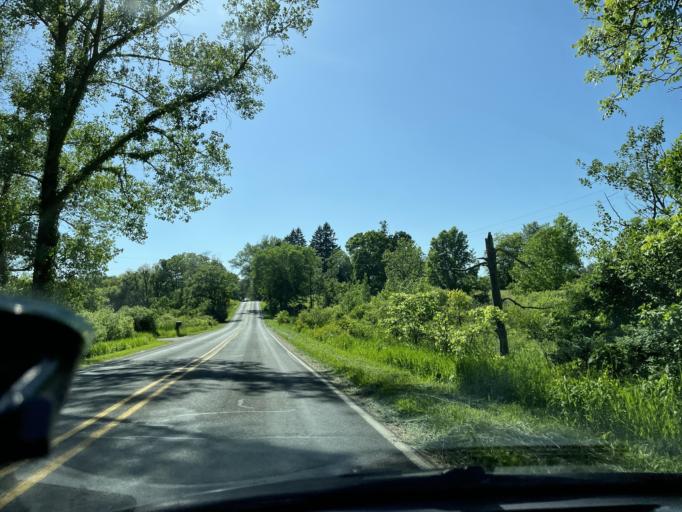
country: US
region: Michigan
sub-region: Barry County
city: Hastings
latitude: 42.6530
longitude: -85.3393
